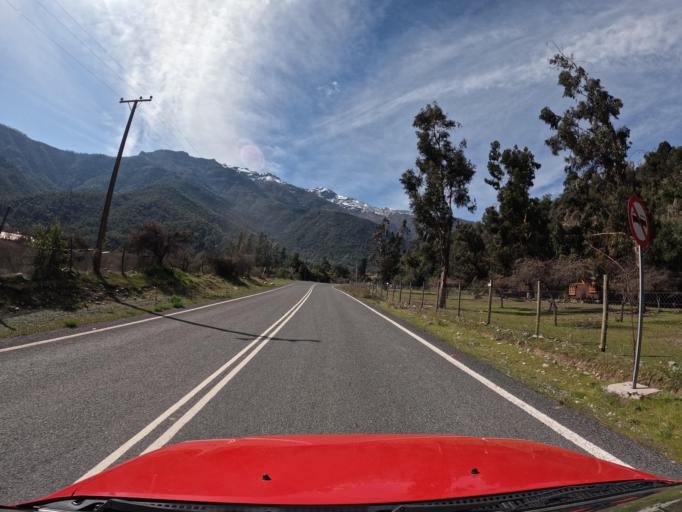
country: CL
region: Maule
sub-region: Provincia de Curico
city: Teno
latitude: -35.0013
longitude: -70.8237
